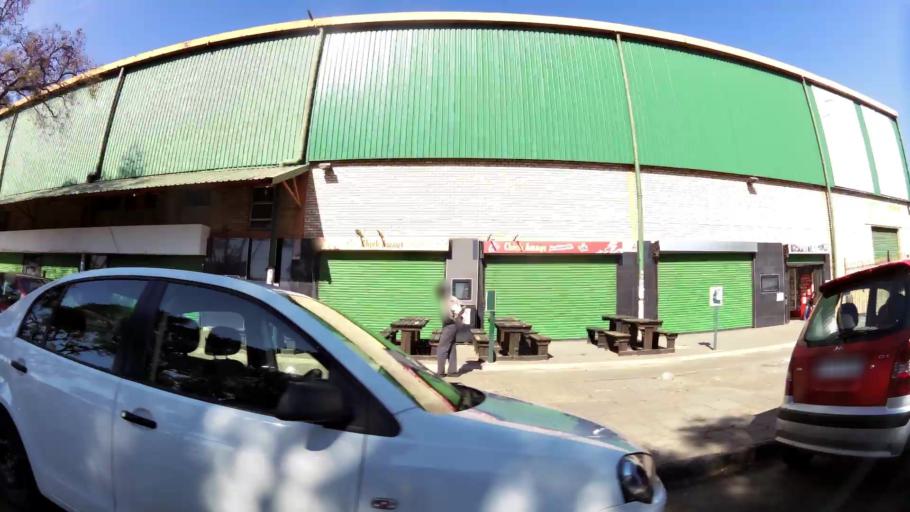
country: ZA
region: Gauteng
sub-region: City of Tshwane Metropolitan Municipality
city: Pretoria
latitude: -25.7407
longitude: 28.1868
